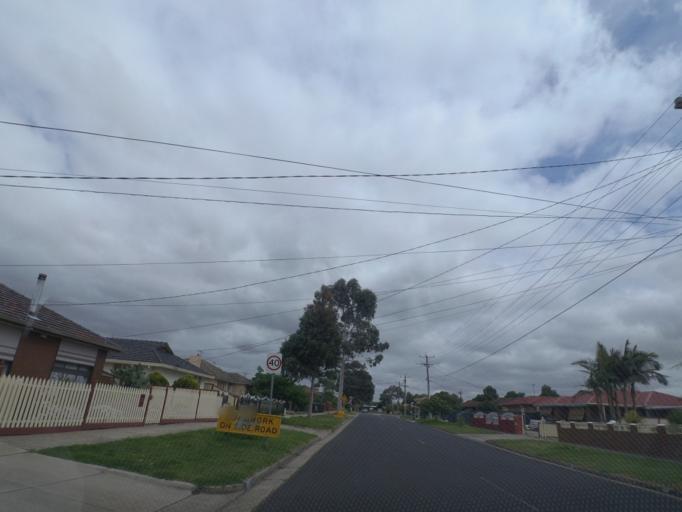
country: AU
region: Victoria
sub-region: Brimbank
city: Deer Park
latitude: -37.7593
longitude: 144.7697
